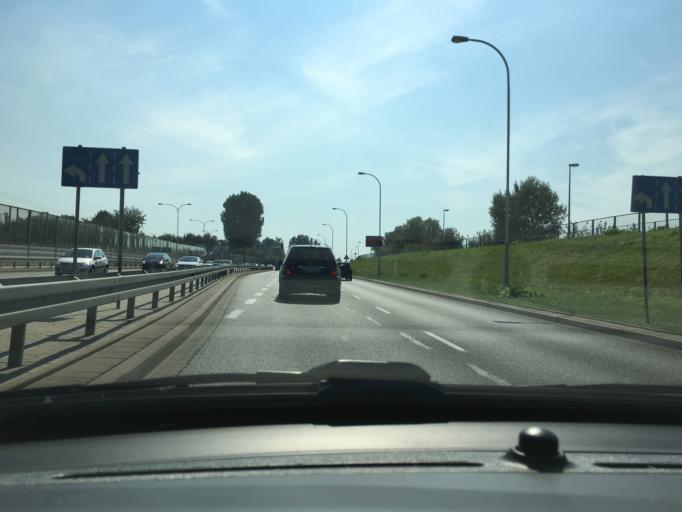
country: PL
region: Masovian Voivodeship
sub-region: Warszawa
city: Wilanow
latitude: 52.2007
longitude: 21.1170
